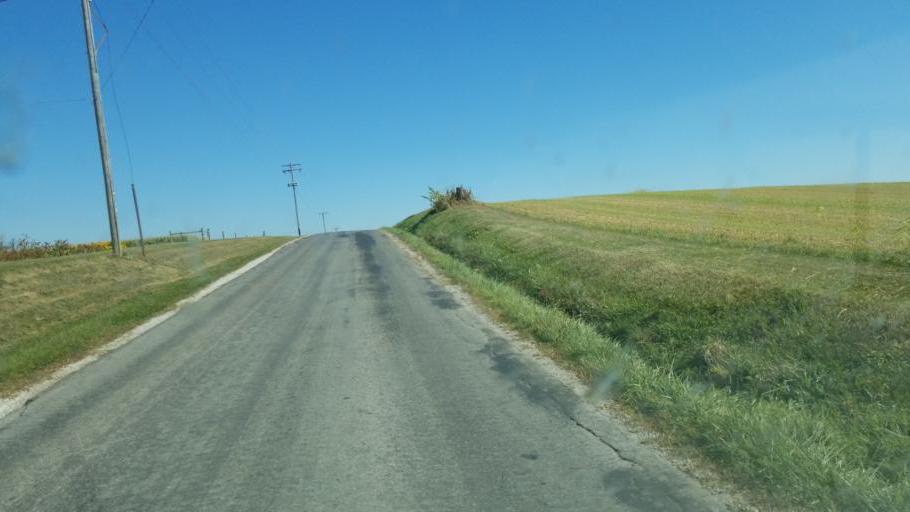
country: US
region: Ohio
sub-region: Huron County
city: Greenwich
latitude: 40.9938
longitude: -82.5570
